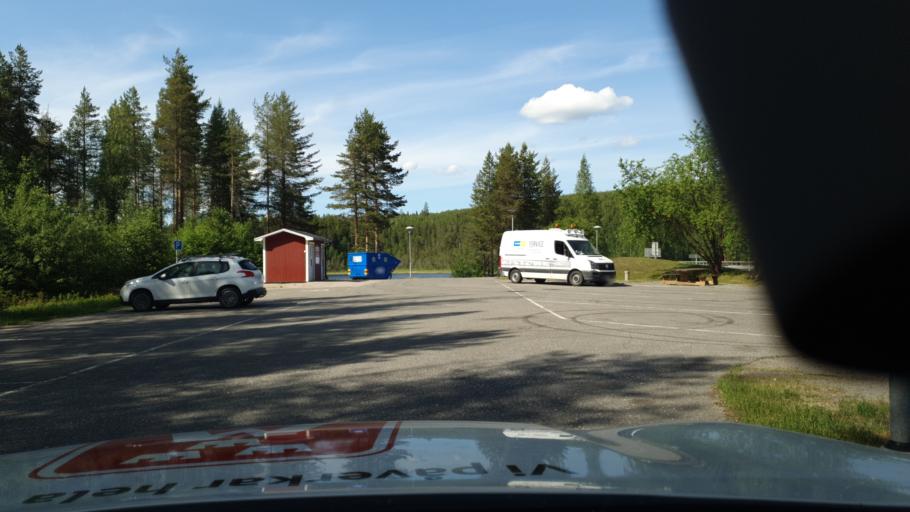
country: SE
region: Vaesterbotten
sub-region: Skelleftea Kommun
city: Boliden
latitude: 64.8954
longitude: 20.3730
